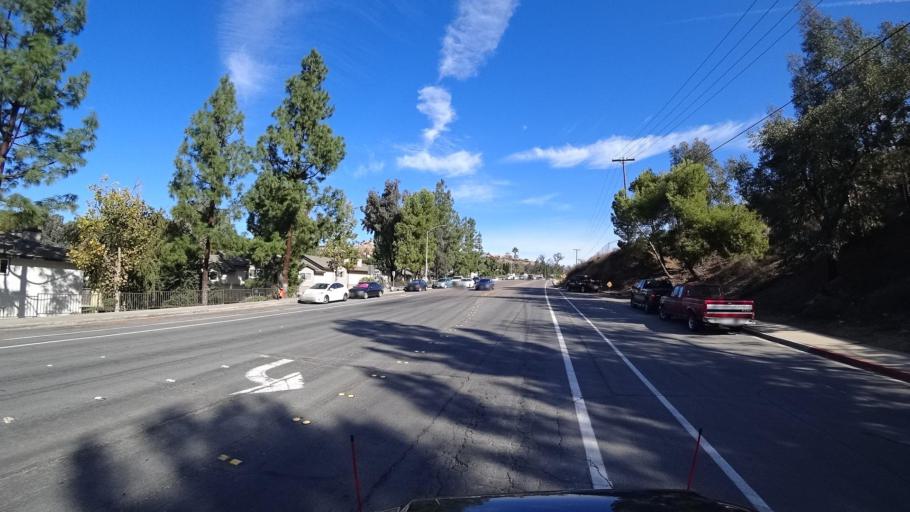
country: US
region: California
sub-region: San Diego County
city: Granite Hills
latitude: 32.8210
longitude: -116.9140
